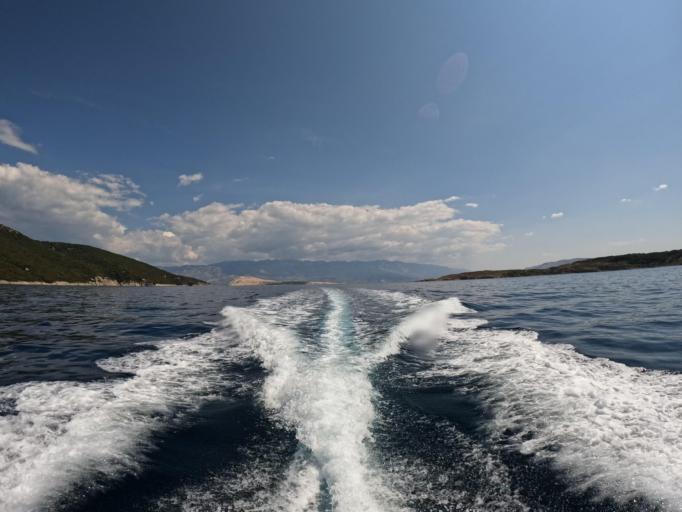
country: HR
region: Primorsko-Goranska
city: Lopar
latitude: 44.8558
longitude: 14.7438
